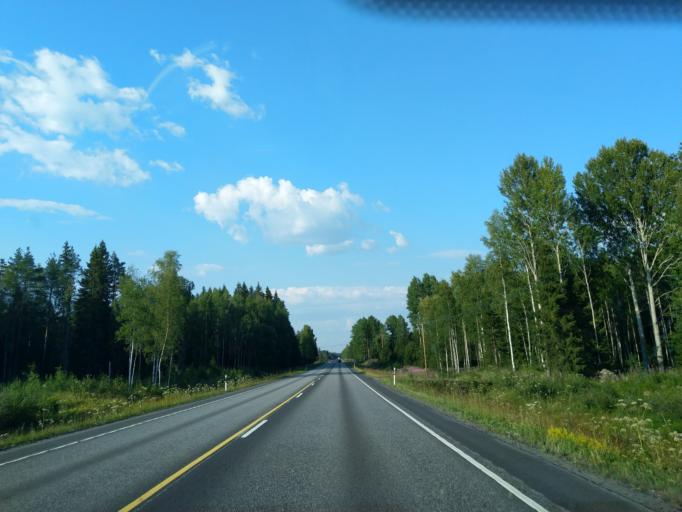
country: FI
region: Satakunta
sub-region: Pori
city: Pomarkku
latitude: 61.7299
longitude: 22.0704
